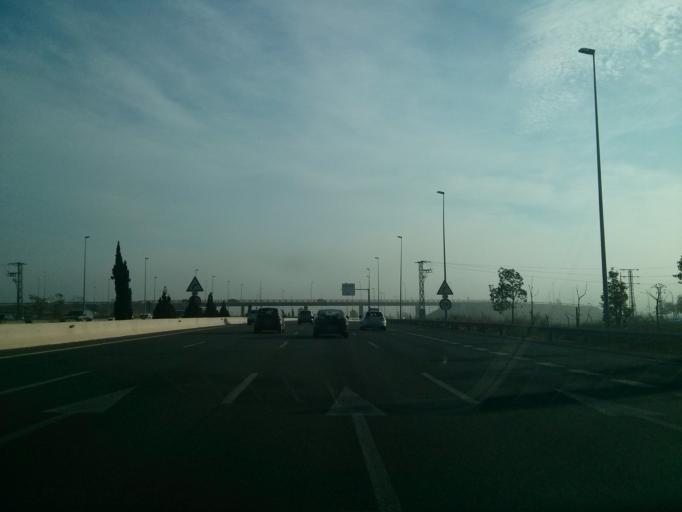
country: ES
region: Valencia
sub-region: Provincia de Valencia
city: Burjassot
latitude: 39.5009
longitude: -0.3973
